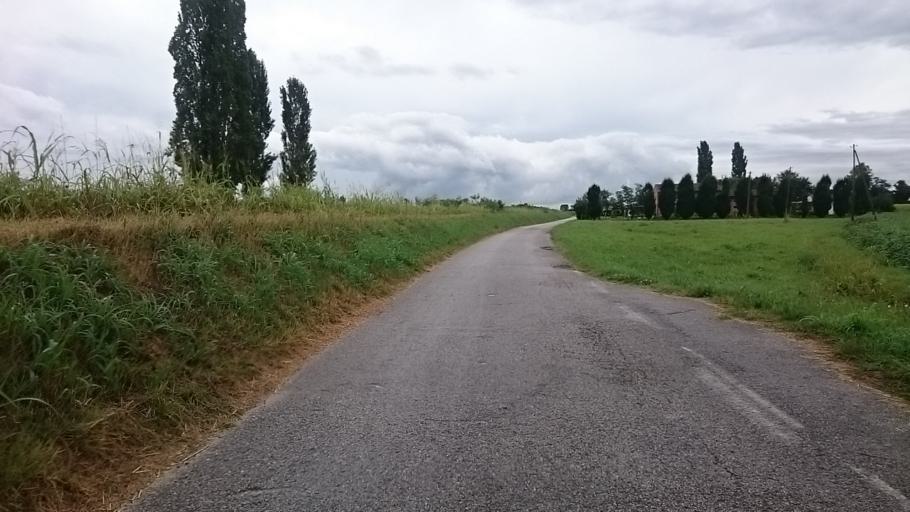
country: IT
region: Veneto
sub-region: Provincia di Padova
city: Loreggiola
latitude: 45.6349
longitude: 11.9245
